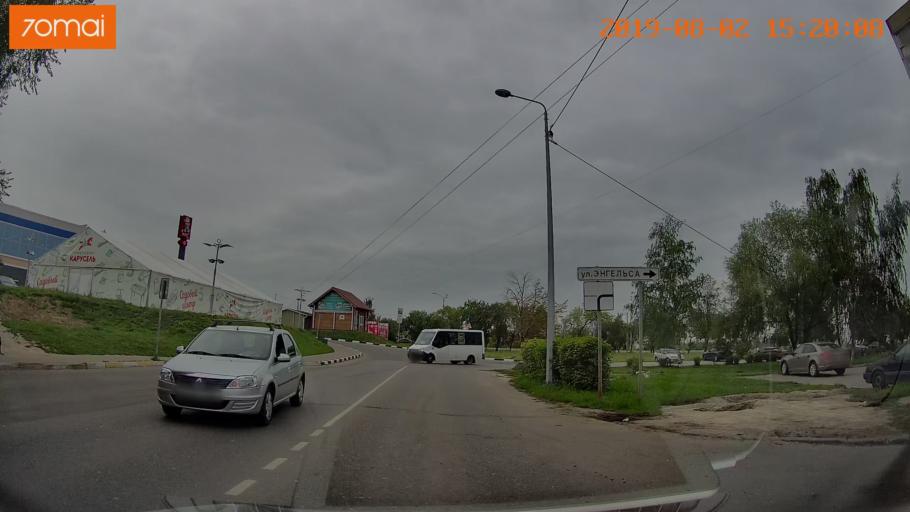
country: RU
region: Moskovskaya
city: Voskresensk
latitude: 55.3141
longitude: 38.6413
